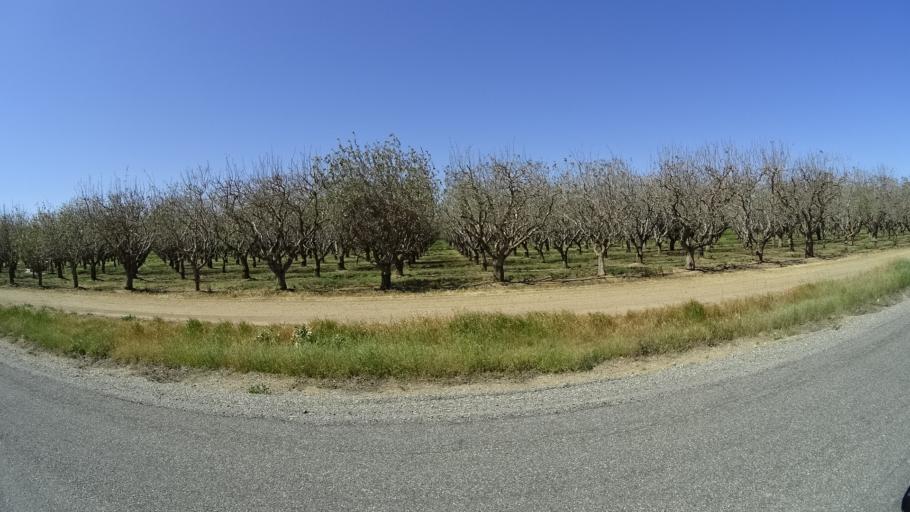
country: US
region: California
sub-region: Glenn County
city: Orland
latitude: 39.7814
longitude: -122.1409
